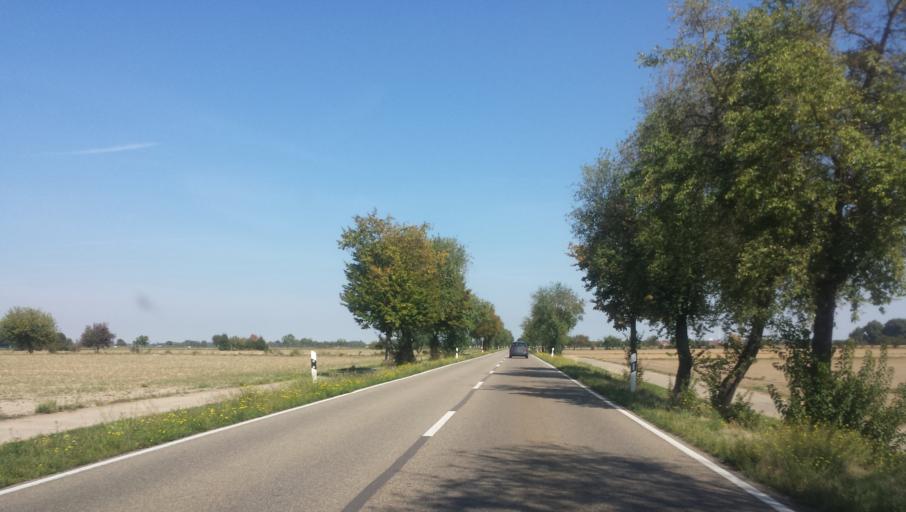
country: DE
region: Rheinland-Pfalz
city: Otterstadt
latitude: 49.3547
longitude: 8.4349
